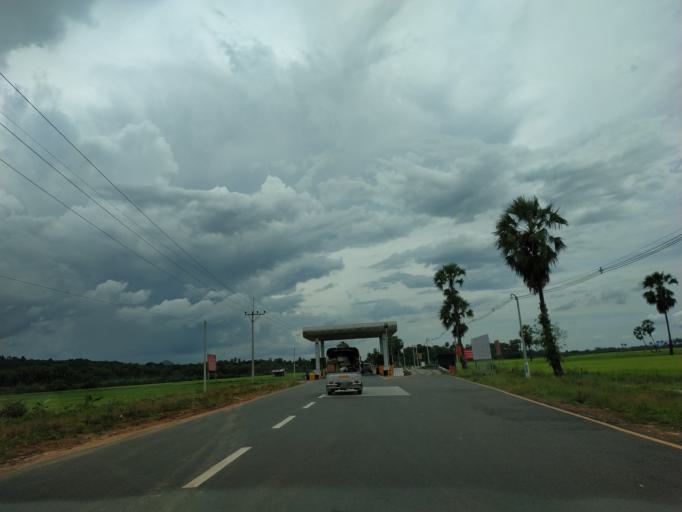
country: MM
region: Tanintharyi
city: Dawei
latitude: 14.0243
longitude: 98.2247
